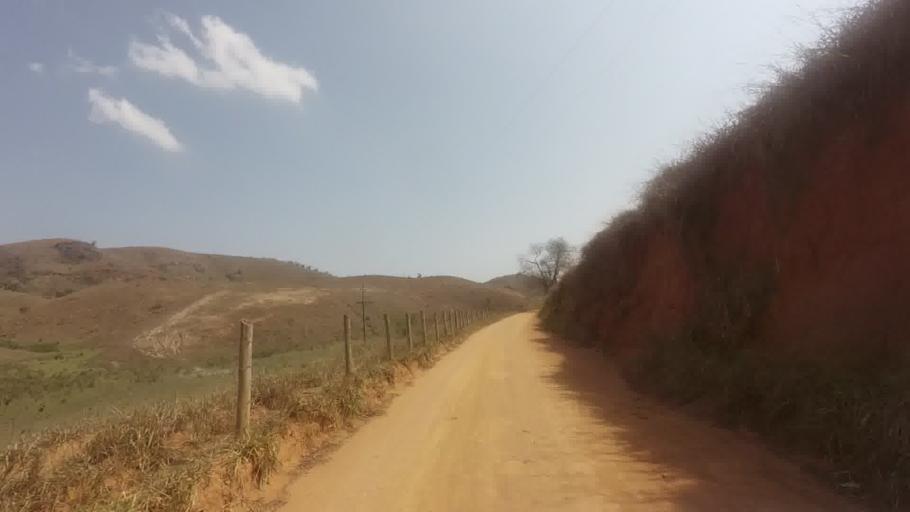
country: BR
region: Espirito Santo
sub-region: Sao Jose Do Calcado
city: Sao Jose do Calcado
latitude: -21.0569
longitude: -41.5342
